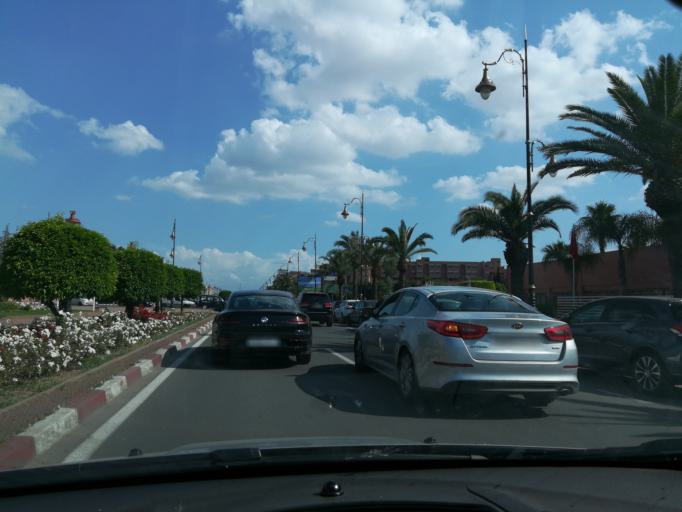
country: MA
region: Marrakech-Tensift-Al Haouz
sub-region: Marrakech
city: Marrakesh
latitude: 31.6278
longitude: -8.0148
